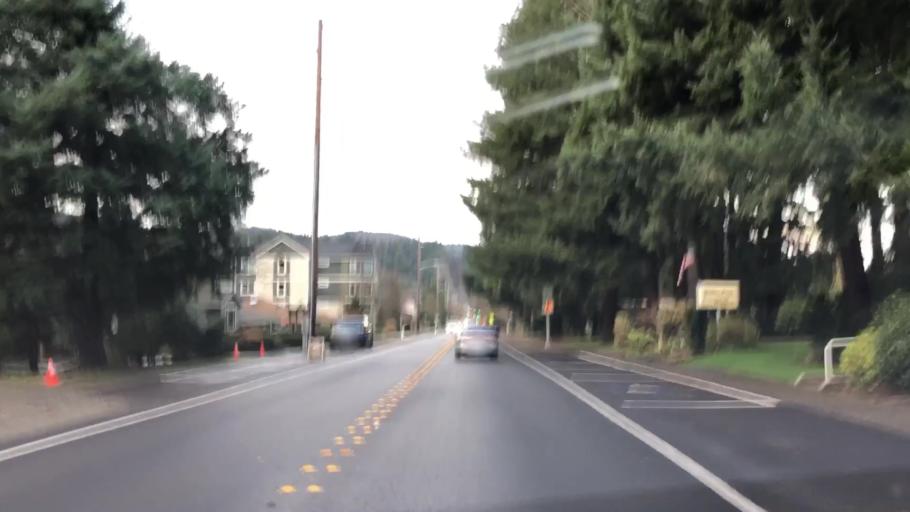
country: US
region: Washington
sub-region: King County
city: Issaquah
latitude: 47.5300
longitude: -122.0273
